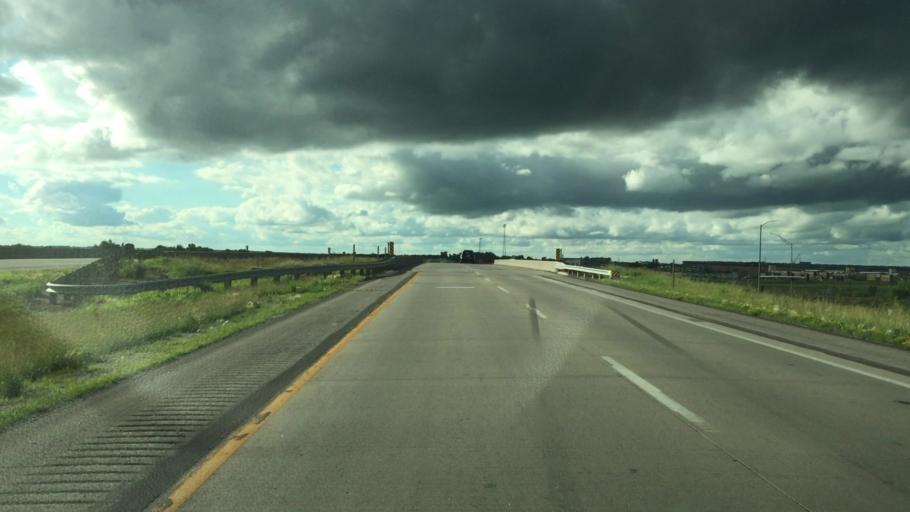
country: US
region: Iowa
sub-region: Polk County
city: Altoona
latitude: 41.6467
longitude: -93.5120
